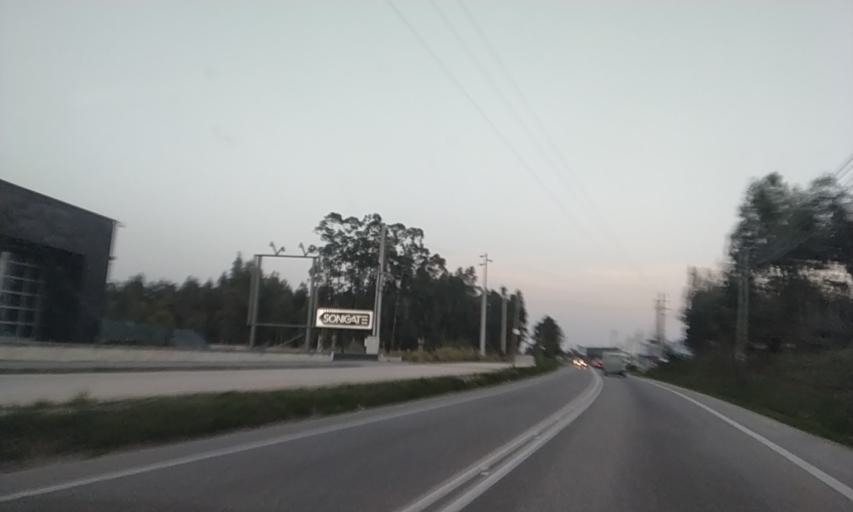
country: PT
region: Leiria
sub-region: Marinha Grande
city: Marinha Grande
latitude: 39.7453
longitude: -8.8744
